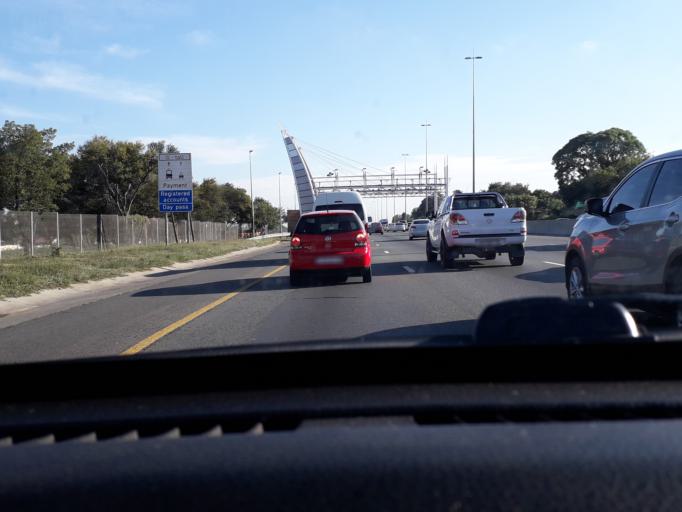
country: ZA
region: Gauteng
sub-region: City of Johannesburg Metropolitan Municipality
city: Roodepoort
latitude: -26.1323
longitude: 27.9378
